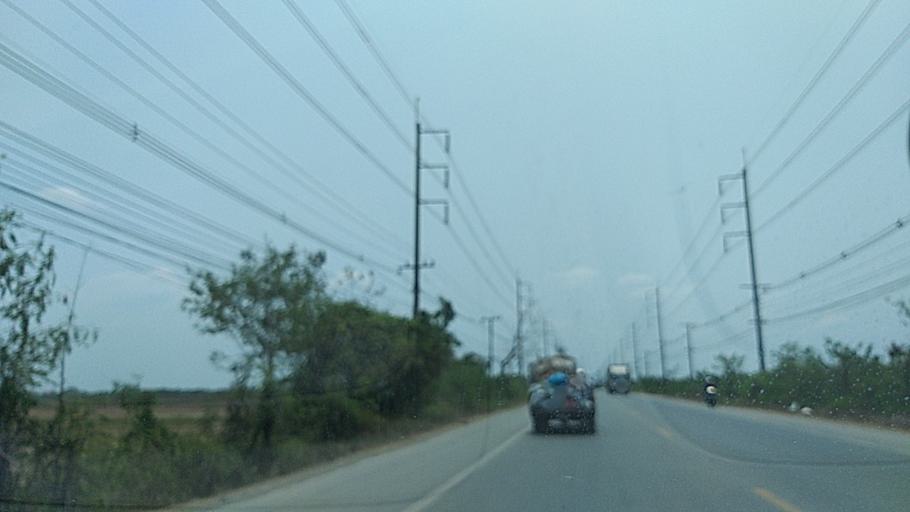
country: TH
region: Chachoengsao
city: Bang Nam Priao
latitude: 13.8121
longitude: 101.0535
